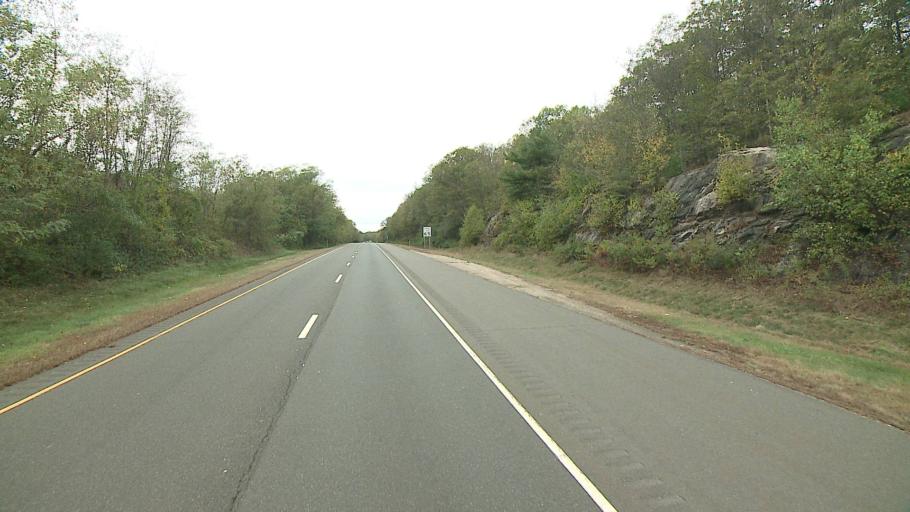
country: US
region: Connecticut
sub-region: Middlesex County
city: Essex Village
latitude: 41.3283
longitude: -72.3865
